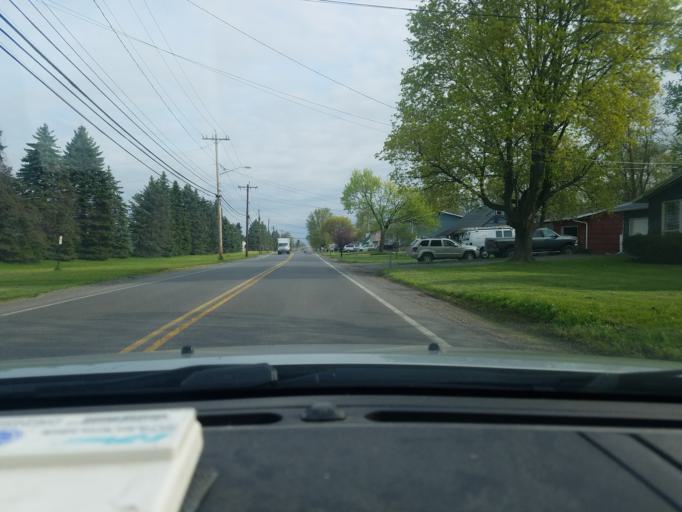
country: US
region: New York
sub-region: Onondaga County
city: East Syracuse
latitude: 43.0805
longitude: -76.0776
